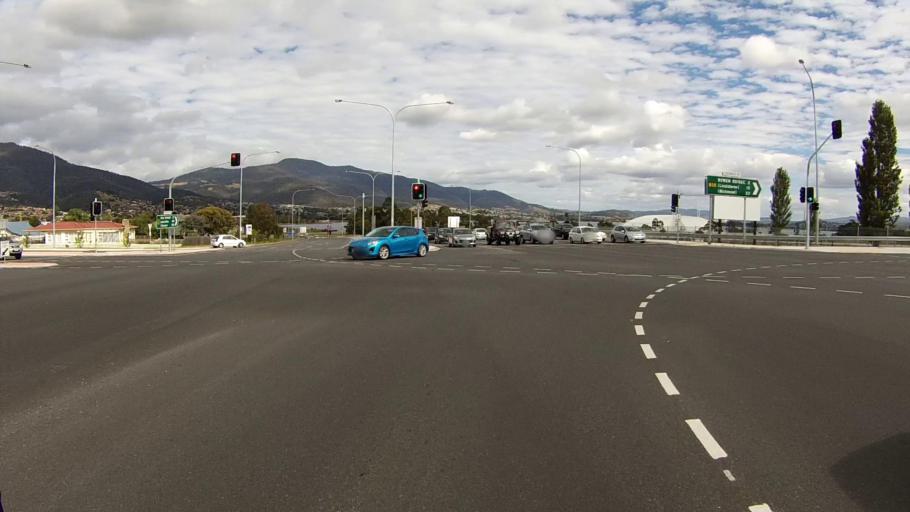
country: AU
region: Tasmania
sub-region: Glenorchy
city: Goodwood
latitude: -42.8279
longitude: 147.2848
